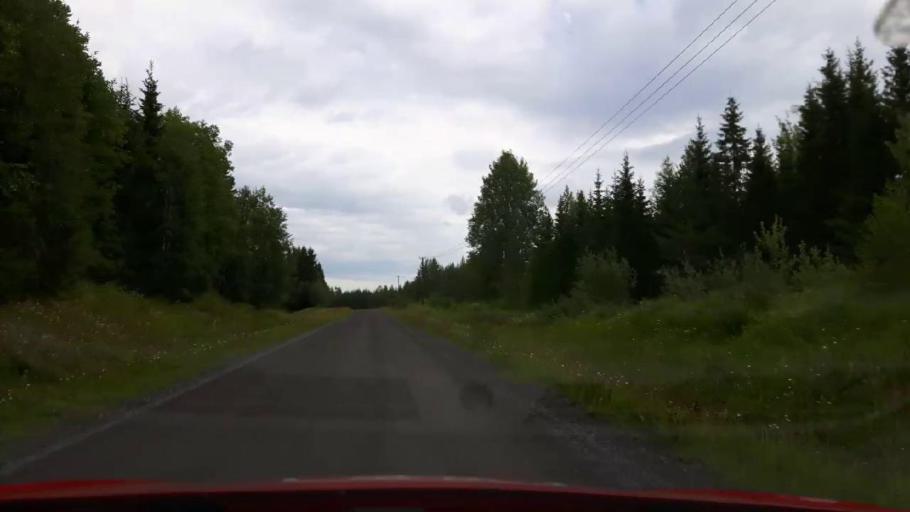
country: SE
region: Jaemtland
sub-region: Stroemsunds Kommun
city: Stroemsund
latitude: 63.4619
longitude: 15.2833
